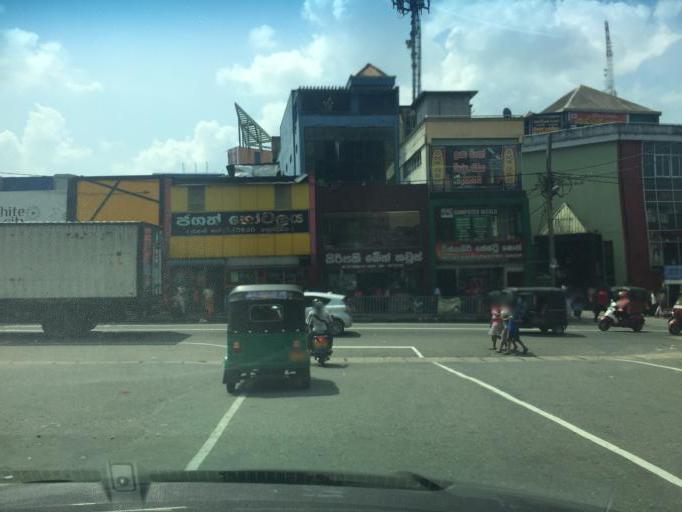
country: LK
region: Western
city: Horana South
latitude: 6.7170
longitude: 80.0630
